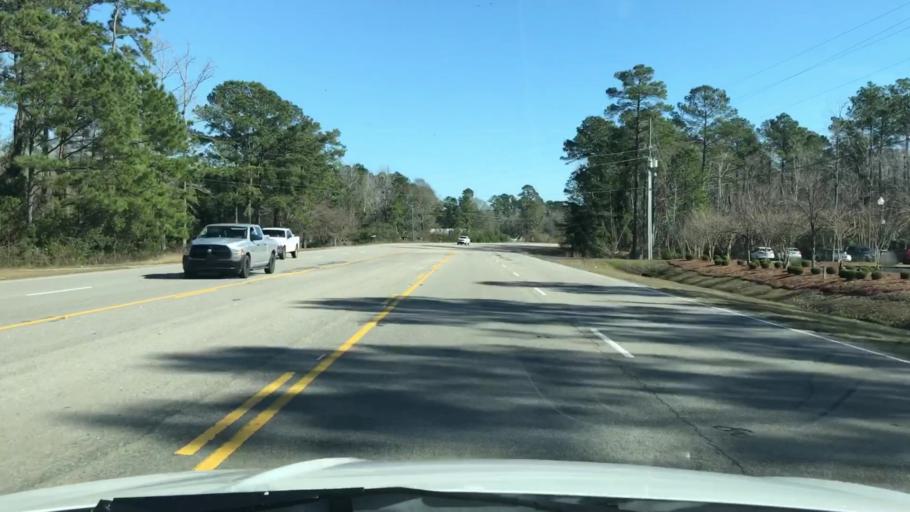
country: US
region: South Carolina
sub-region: Horry County
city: Garden City
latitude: 33.6303
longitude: -79.0223
